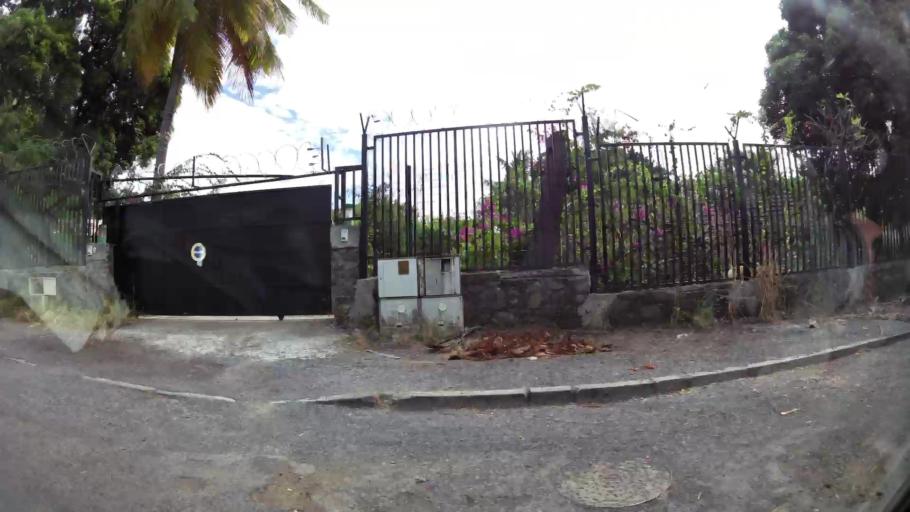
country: YT
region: Mamoudzou
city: Mamoudzou
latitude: -12.7769
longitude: 45.2284
